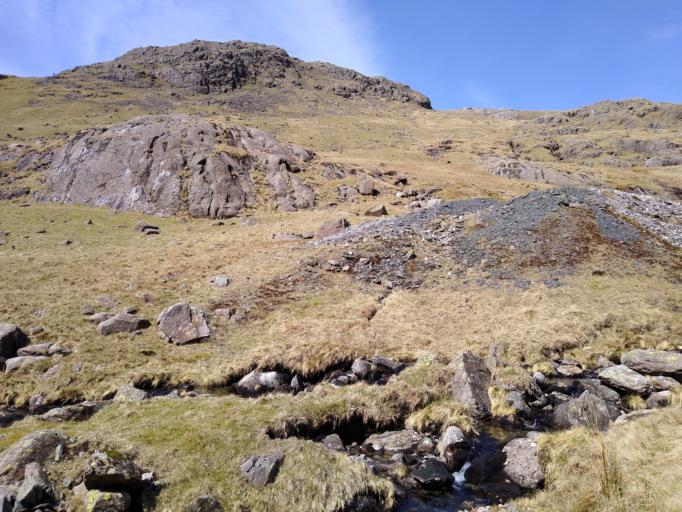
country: GB
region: England
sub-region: Cumbria
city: Ambleside
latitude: 54.3869
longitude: -3.1310
